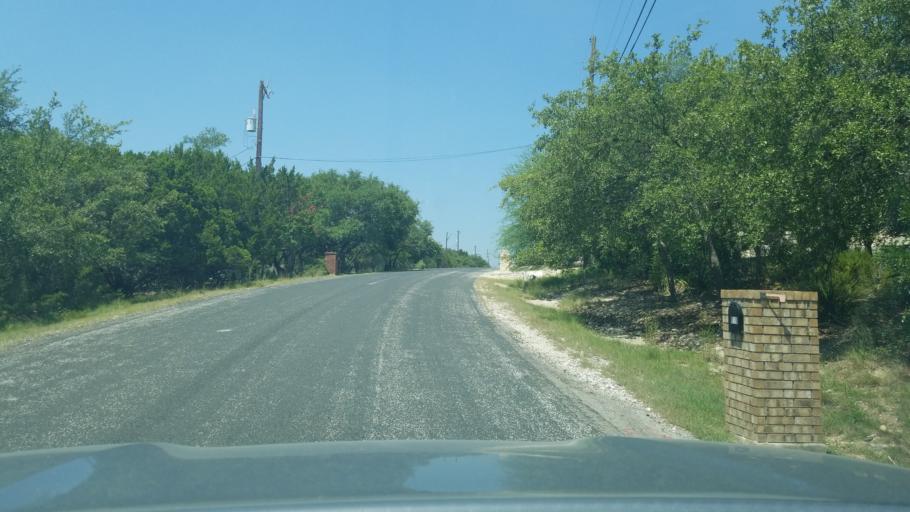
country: US
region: Texas
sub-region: Bexar County
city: Timberwood Park
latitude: 29.6920
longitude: -98.4811
